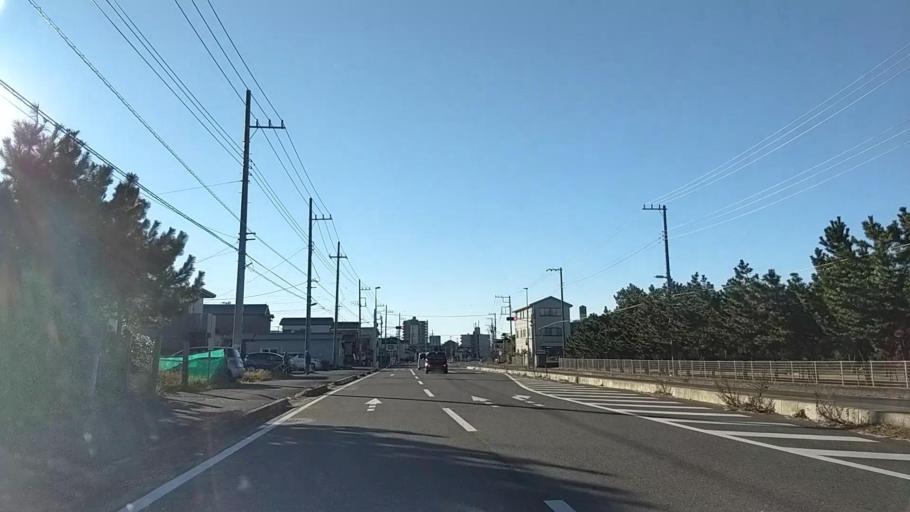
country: JP
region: Chiba
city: Kisarazu
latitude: 35.3889
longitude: 139.9199
